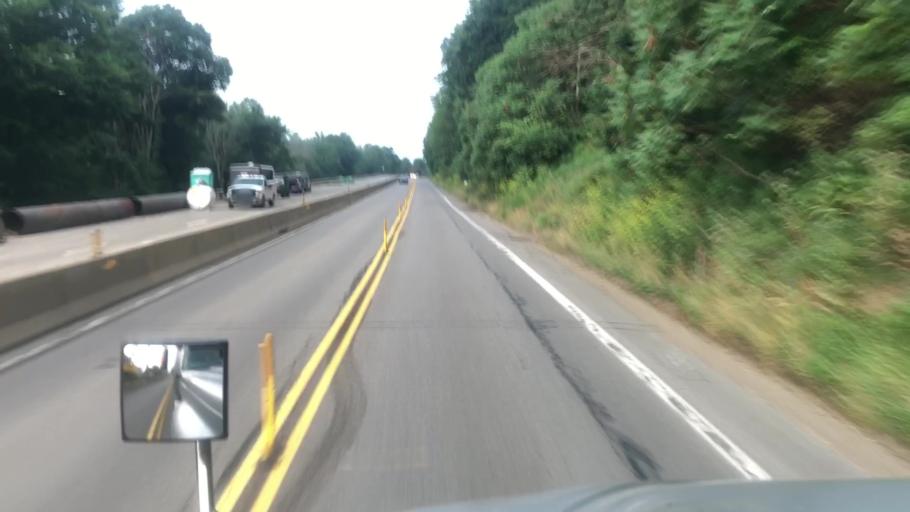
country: US
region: Pennsylvania
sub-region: Venango County
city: Woodland Heights
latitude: 41.4172
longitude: -79.7321
